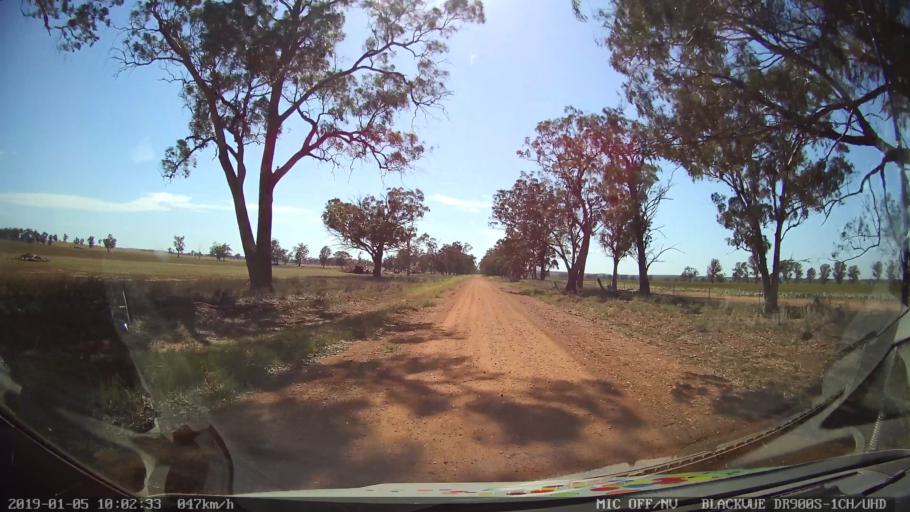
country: AU
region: New South Wales
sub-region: Gilgandra
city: Gilgandra
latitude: -31.6708
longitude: 148.8442
